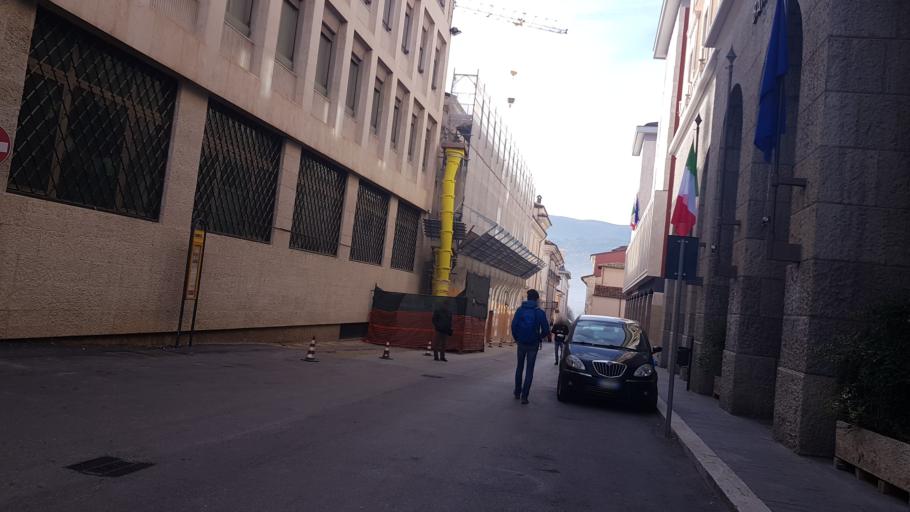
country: IT
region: Abruzzo
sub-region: Provincia dell' Aquila
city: L'Aquila
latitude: 42.3484
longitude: 13.3986
